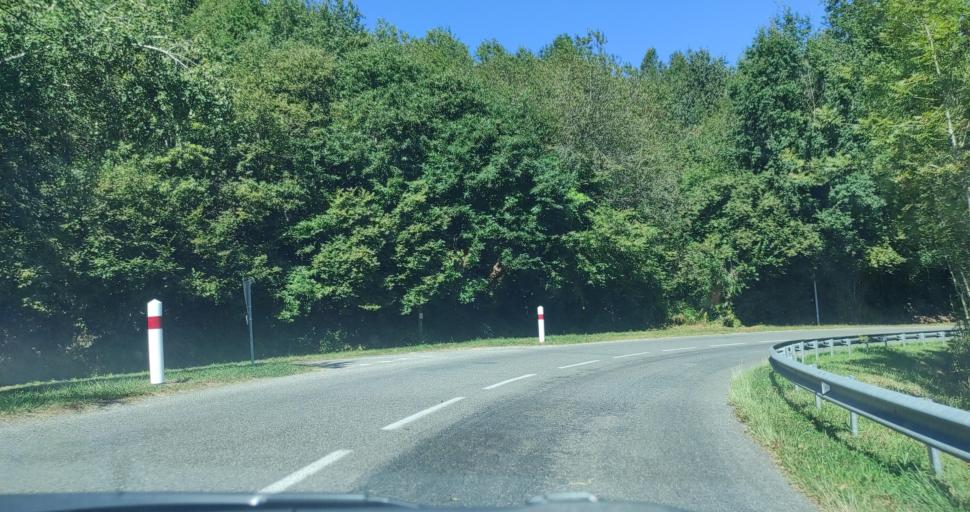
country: FR
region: Midi-Pyrenees
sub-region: Departement de l'Aveyron
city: Firmi
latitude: 44.5188
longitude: 2.3055
